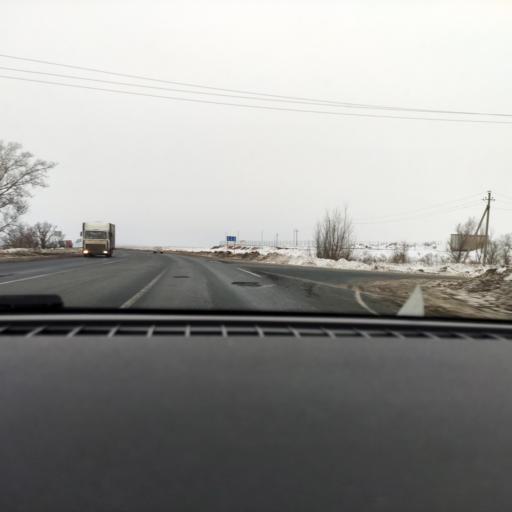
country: RU
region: Samara
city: Novosemeykino
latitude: 53.3953
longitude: 50.4262
